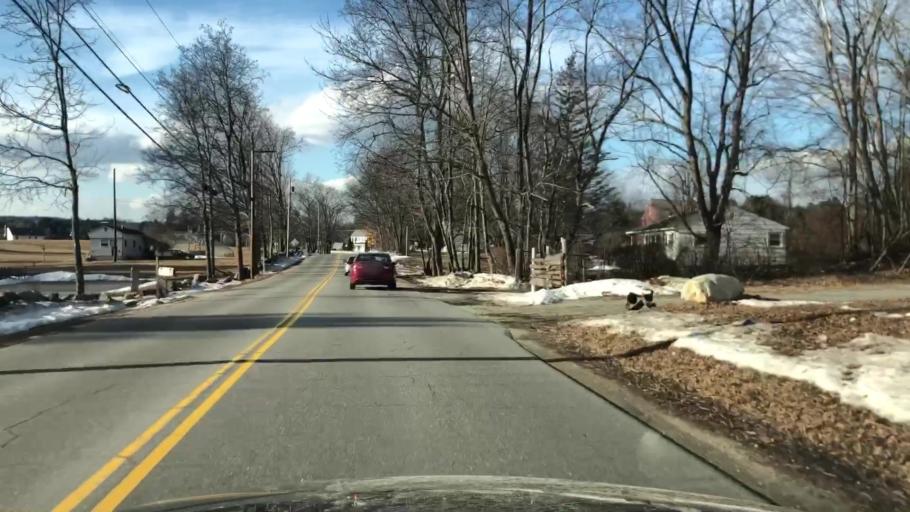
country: US
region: New Hampshire
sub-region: Hillsborough County
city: Milford
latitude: 42.8468
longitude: -71.6688
